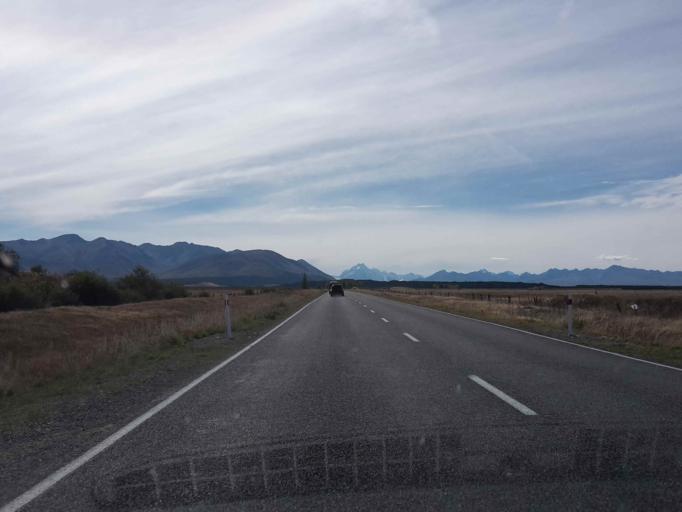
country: NZ
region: Canterbury
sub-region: Timaru District
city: Pleasant Point
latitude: -44.2330
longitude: 170.1164
